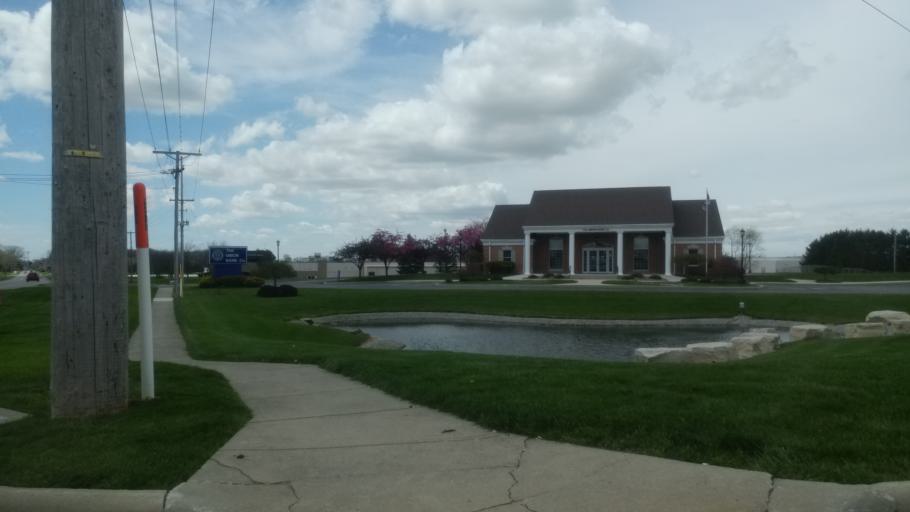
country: US
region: Ohio
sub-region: Hancock County
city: Findlay
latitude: 41.0592
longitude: -83.6164
